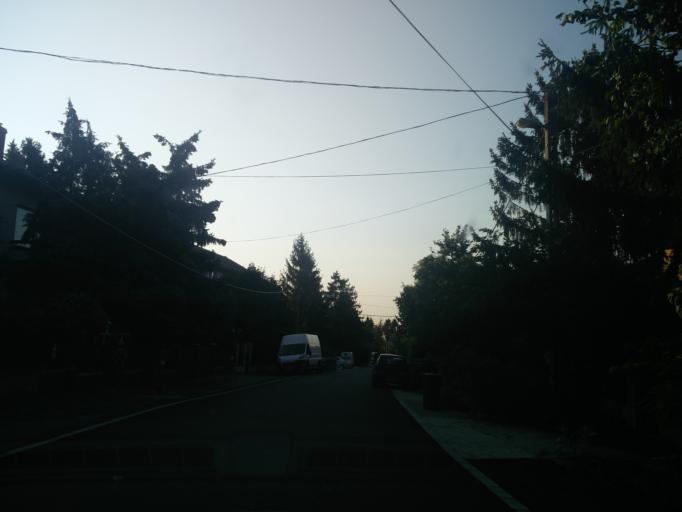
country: HU
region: Budapest
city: Budapest XII. keruelet
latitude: 47.4764
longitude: 19.0010
